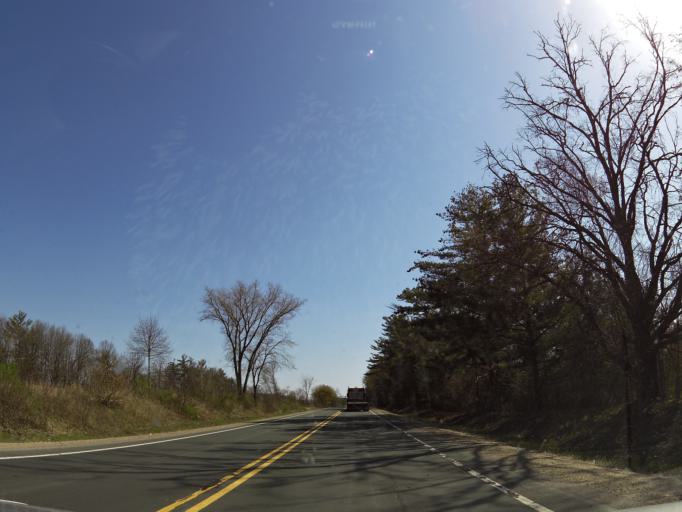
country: US
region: Wisconsin
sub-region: Pepin County
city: Durand
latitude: 44.7415
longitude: -91.9331
